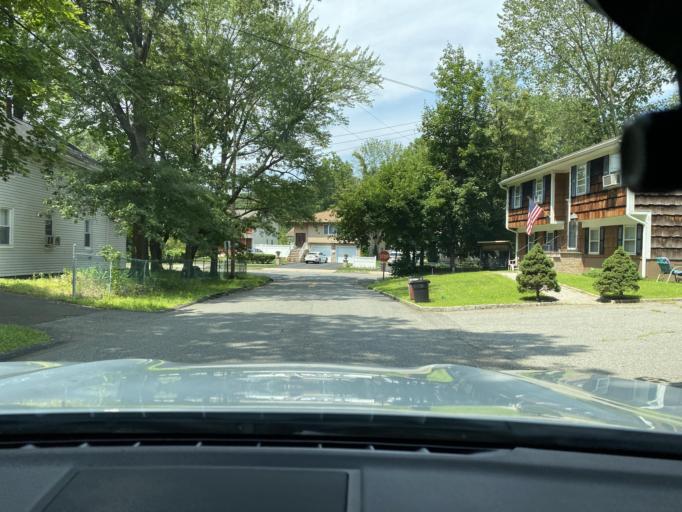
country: US
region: New York
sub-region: Rockland County
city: Suffern
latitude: 41.1008
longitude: -74.1549
